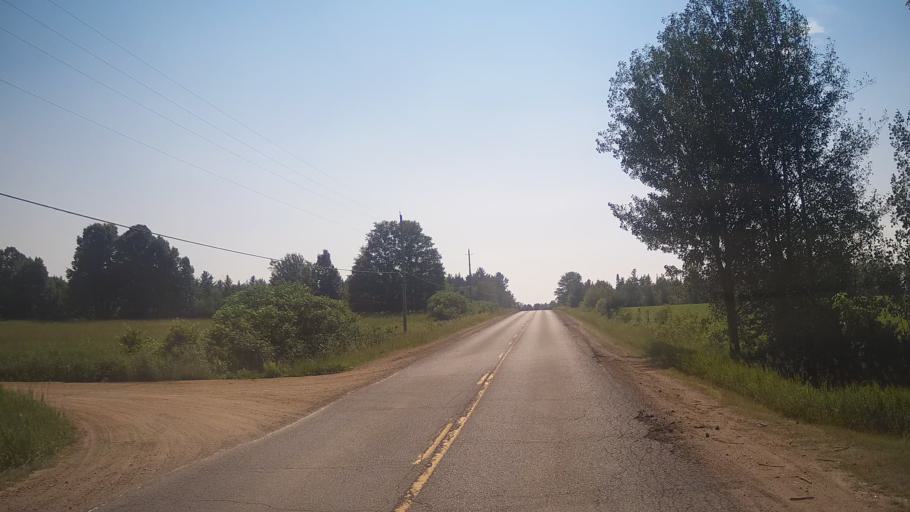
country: CA
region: Ontario
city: Pembroke
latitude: 45.6047
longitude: -77.2246
